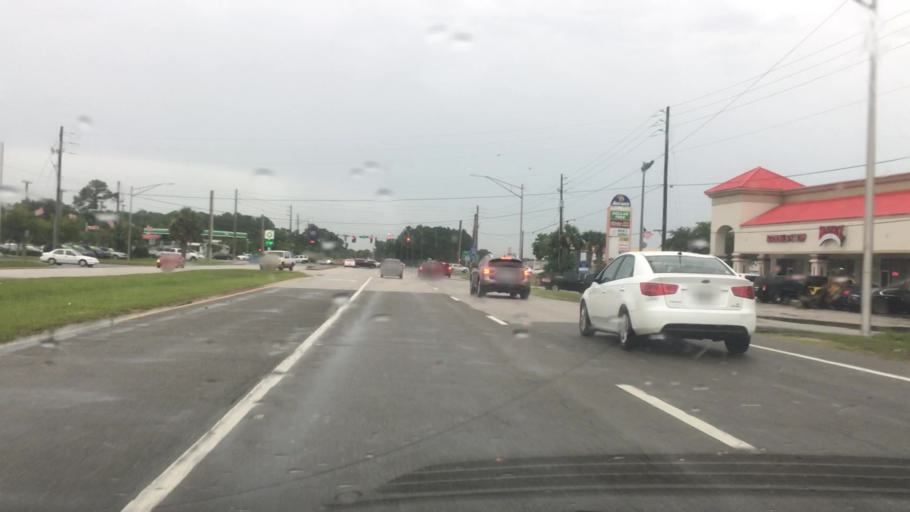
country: US
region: Florida
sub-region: Duval County
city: Atlantic Beach
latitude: 30.3228
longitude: -81.5230
